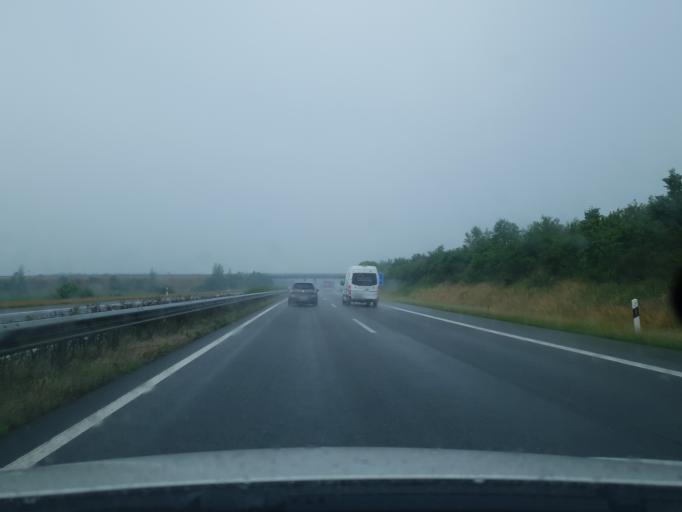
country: DE
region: Lower Saxony
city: Emsburen
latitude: 52.3775
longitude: 7.2476
